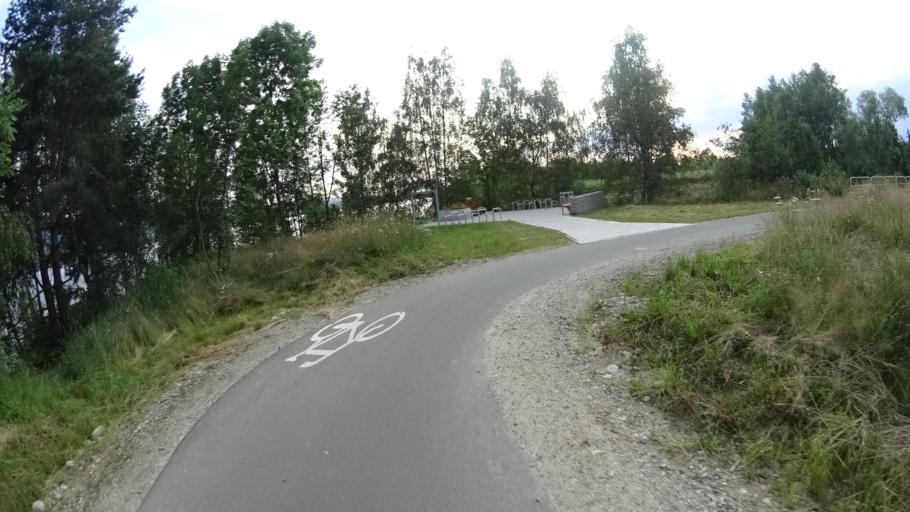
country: PL
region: Lesser Poland Voivodeship
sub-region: Powiat nowotarski
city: Maniowy
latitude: 49.4533
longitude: 20.2583
